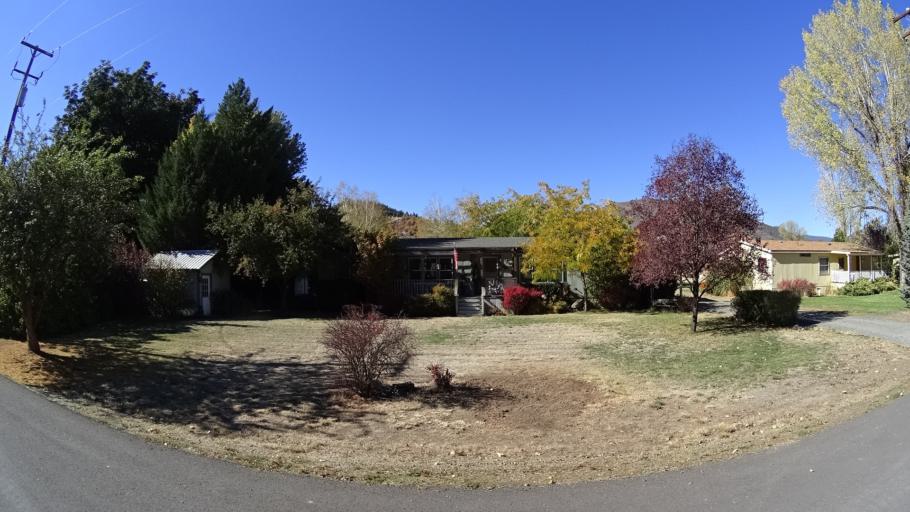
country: US
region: California
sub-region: Siskiyou County
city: Yreka
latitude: 41.6188
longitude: -122.8344
